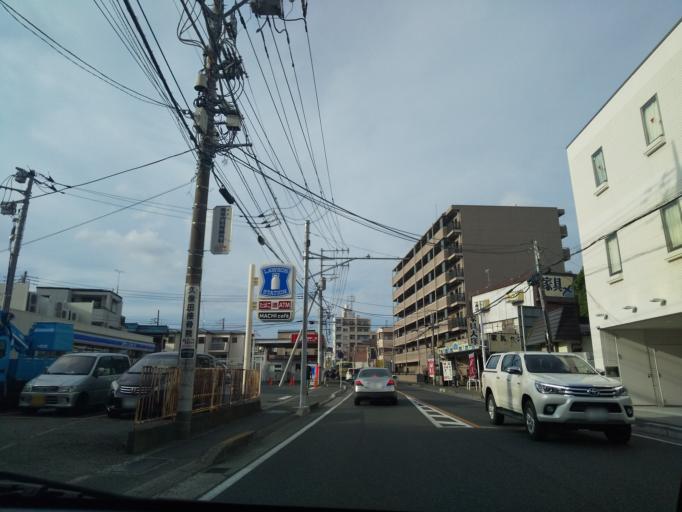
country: JP
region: Kanagawa
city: Zama
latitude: 35.5011
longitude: 139.4093
